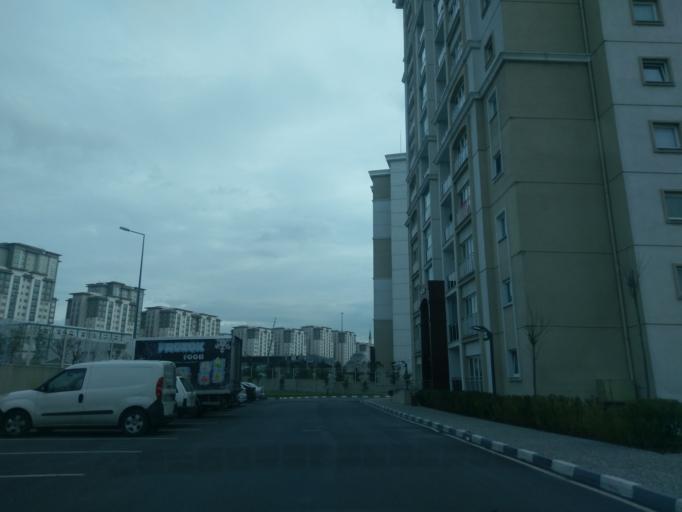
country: TR
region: Istanbul
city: Esenyurt
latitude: 41.0892
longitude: 28.6517
